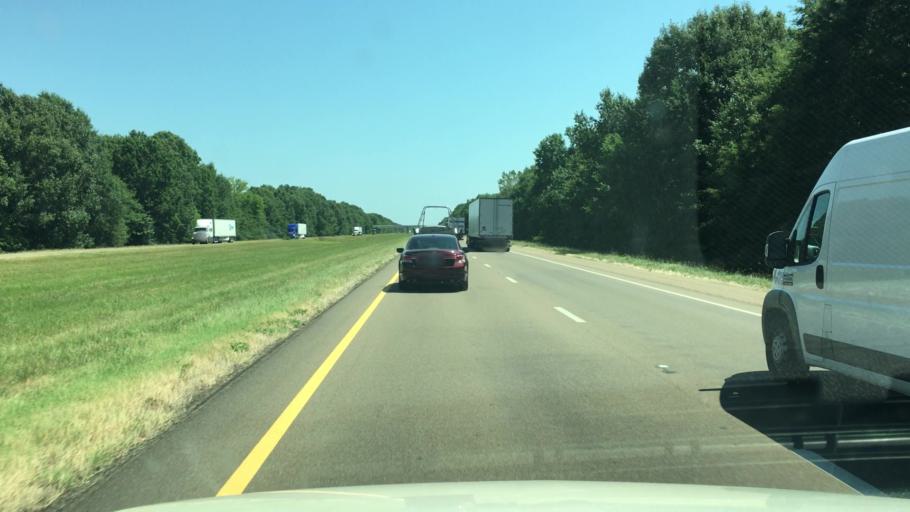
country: US
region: Texas
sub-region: Morris County
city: Naples
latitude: 33.3296
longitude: -94.6750
